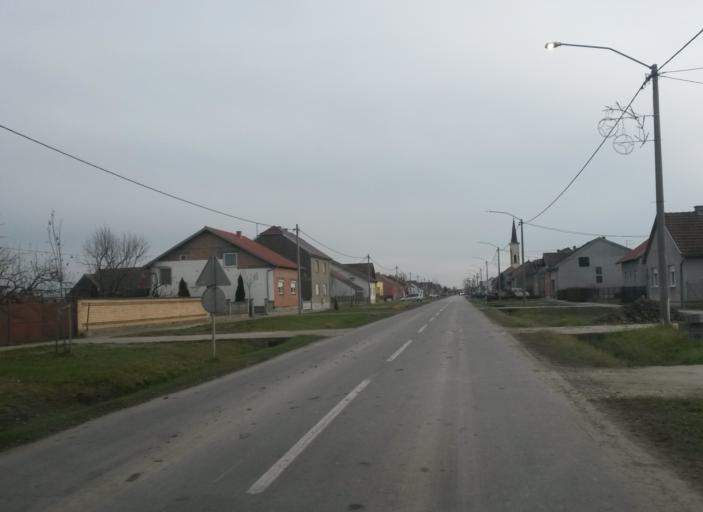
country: HR
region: Osjecko-Baranjska
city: Antunovac
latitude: 45.4876
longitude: 18.6332
